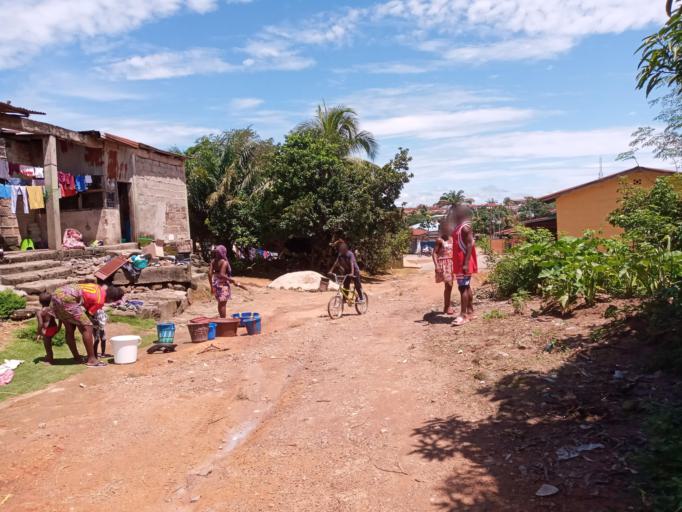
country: SL
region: Eastern Province
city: Koidu
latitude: 8.6398
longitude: -10.9738
